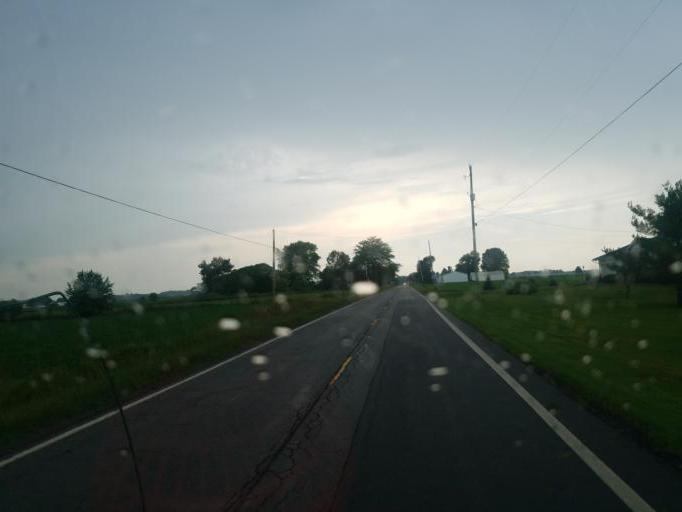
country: US
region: Ohio
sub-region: Wayne County
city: Rittman
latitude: 40.9457
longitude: -81.8158
